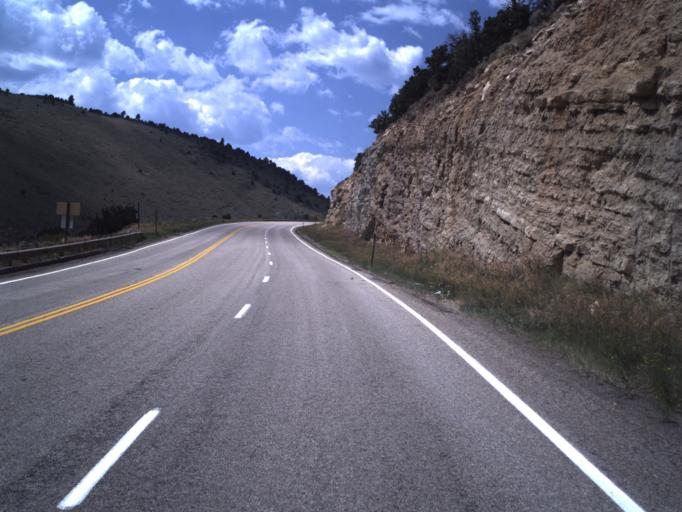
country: US
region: Utah
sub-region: Daggett County
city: Manila
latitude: 40.9063
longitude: -109.6996
